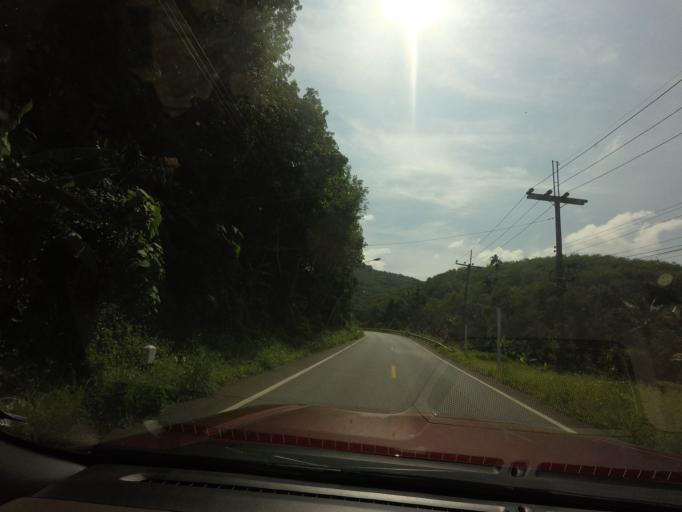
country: TH
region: Yala
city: Betong
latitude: 5.8175
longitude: 101.0732
